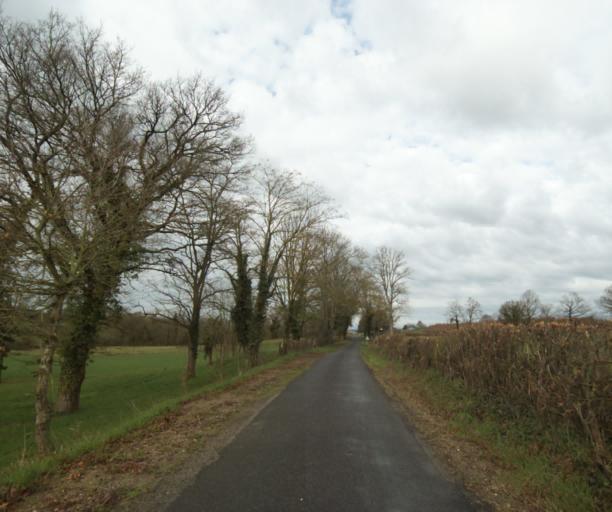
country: FR
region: Auvergne
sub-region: Departement de l'Allier
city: Toulon-sur-Allier
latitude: 46.5141
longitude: 3.3738
